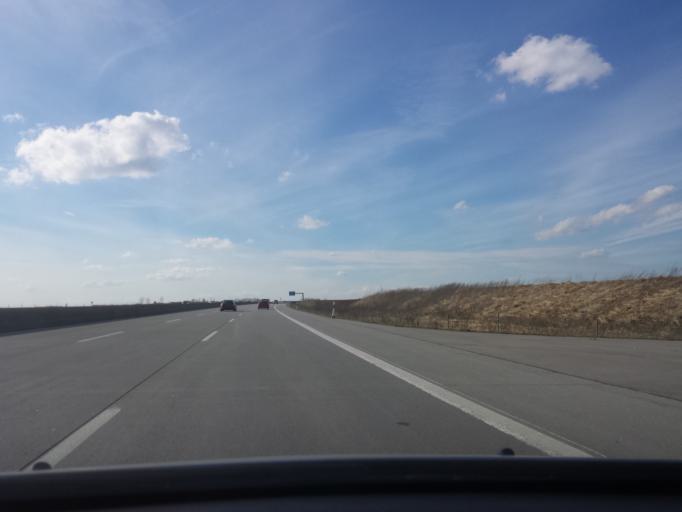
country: DE
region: Bavaria
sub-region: Upper Bavaria
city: Odelzhausen
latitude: 48.2980
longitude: 11.2234
